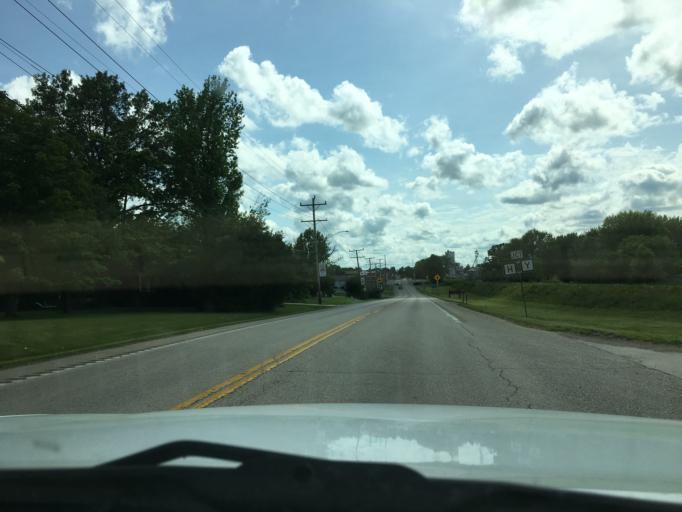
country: US
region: Missouri
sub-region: Franklin County
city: Gerald
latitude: 38.4042
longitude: -91.3263
